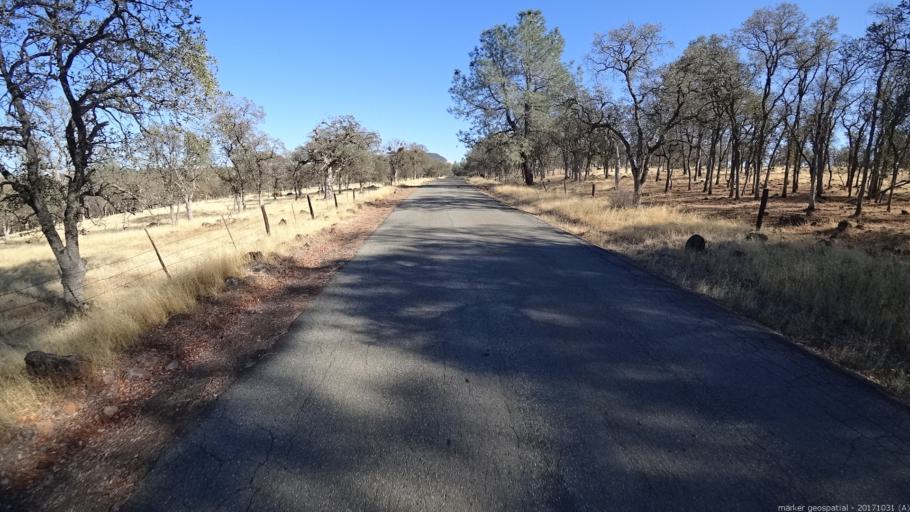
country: US
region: California
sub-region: Shasta County
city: Shingletown
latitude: 40.4586
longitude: -122.0427
